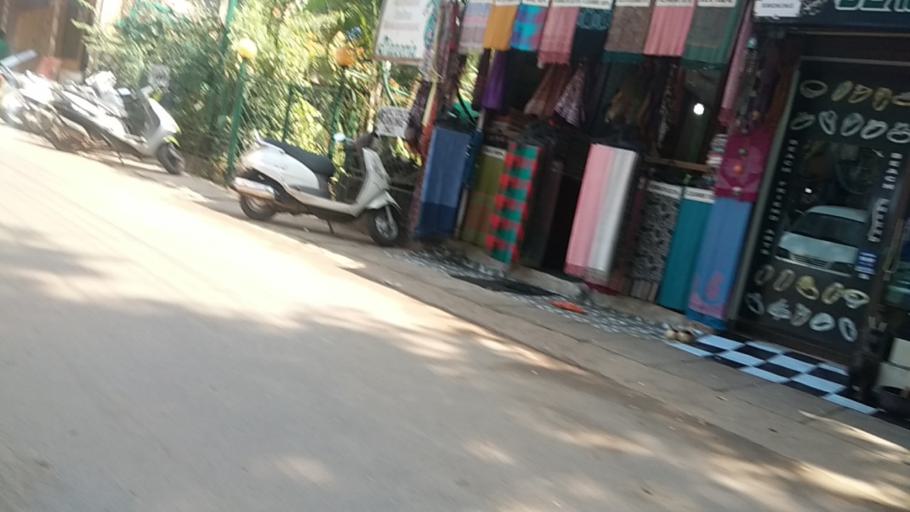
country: IN
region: Goa
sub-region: South Goa
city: Kankon
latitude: 15.0126
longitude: 74.0221
